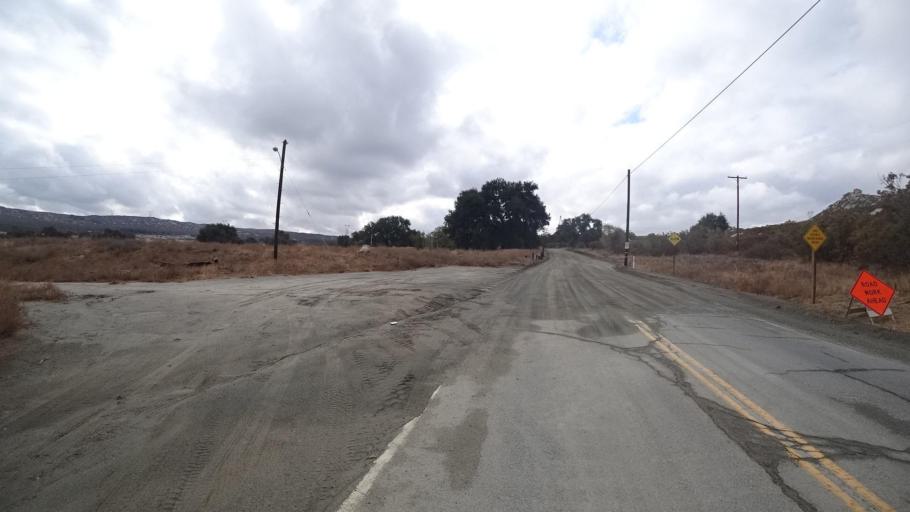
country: US
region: California
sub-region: San Diego County
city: Campo
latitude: 32.6006
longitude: -116.4698
